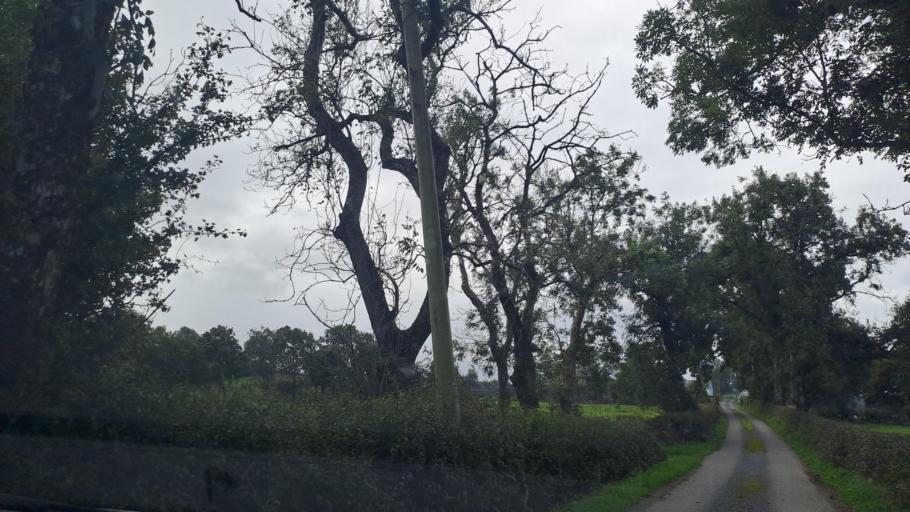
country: IE
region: Ulster
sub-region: An Cabhan
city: Kingscourt
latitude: 53.9803
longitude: -6.8386
